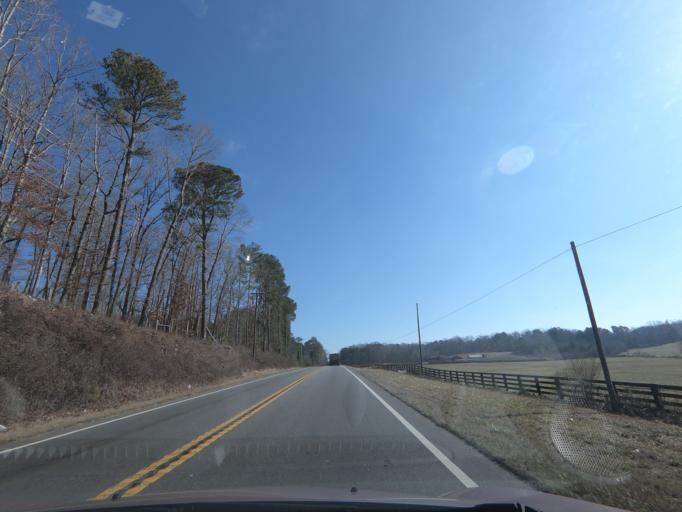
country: US
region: Georgia
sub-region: Forsyth County
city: Cumming
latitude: 34.3006
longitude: -84.2290
